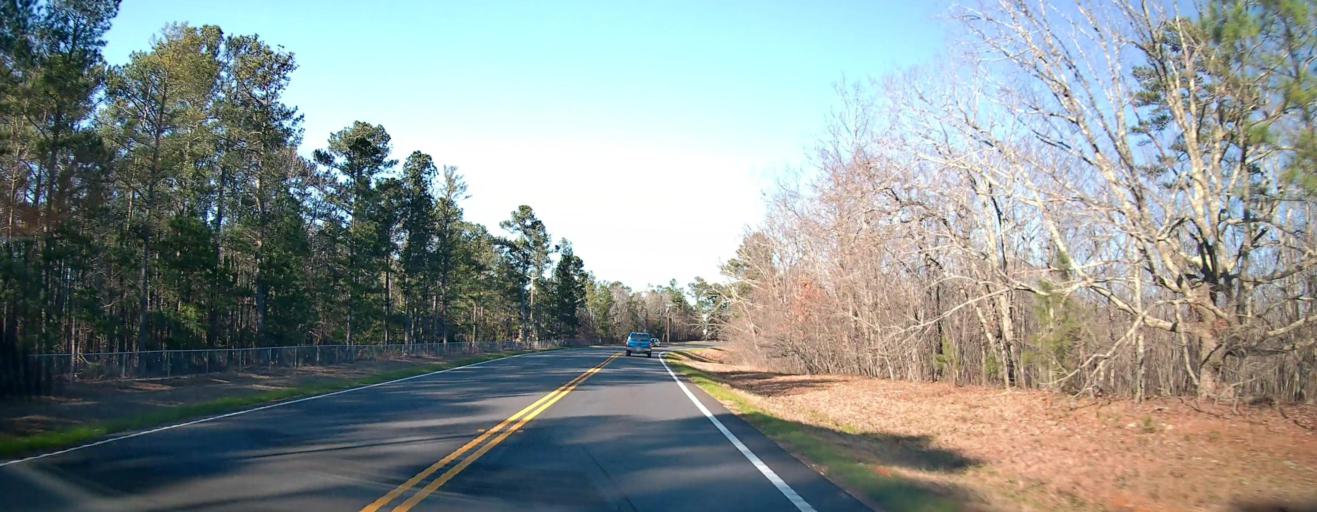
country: US
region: Georgia
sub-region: Meriwether County
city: Manchester
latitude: 32.8536
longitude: -84.6997
